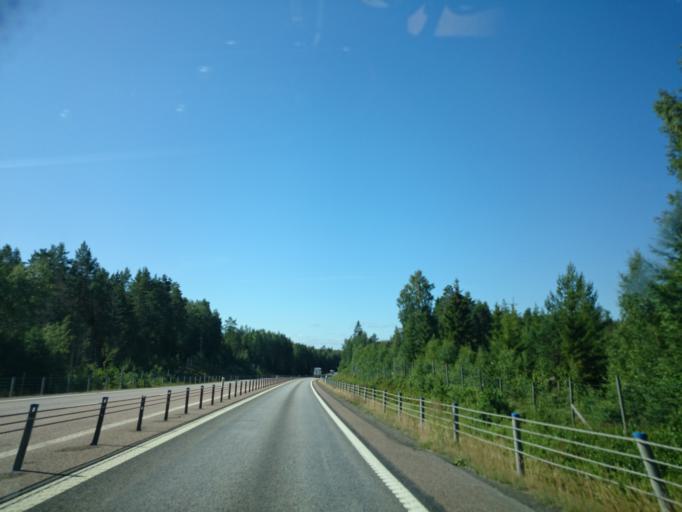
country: SE
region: Gaevleborg
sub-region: Soderhamns Kommun
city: Ljusne
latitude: 61.1434
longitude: 17.0310
